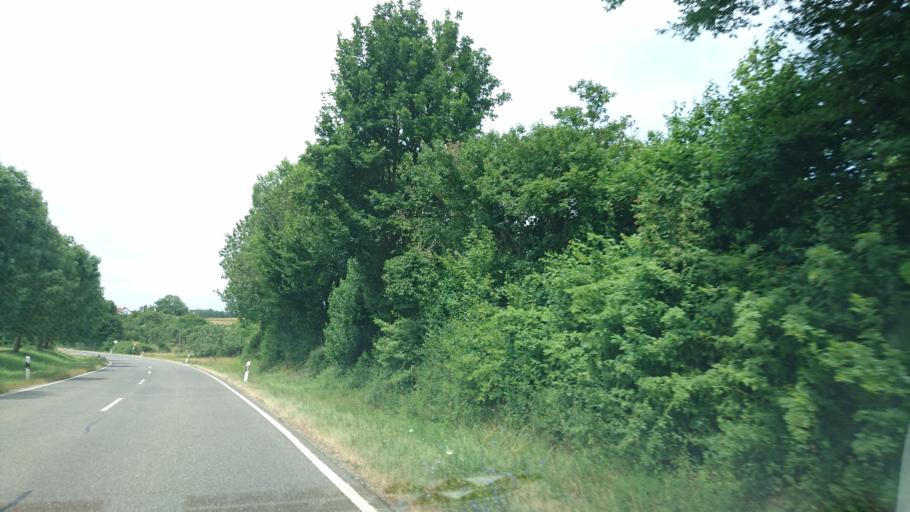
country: DE
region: Bavaria
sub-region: Regierungsbezirk Mittelfranken
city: Thalmassing
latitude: 49.1112
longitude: 11.1797
